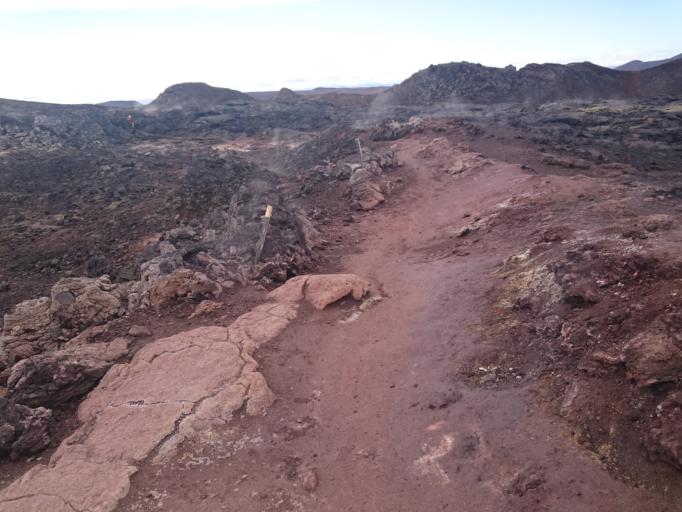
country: IS
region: Northeast
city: Laugar
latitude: 65.7216
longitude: -16.7932
